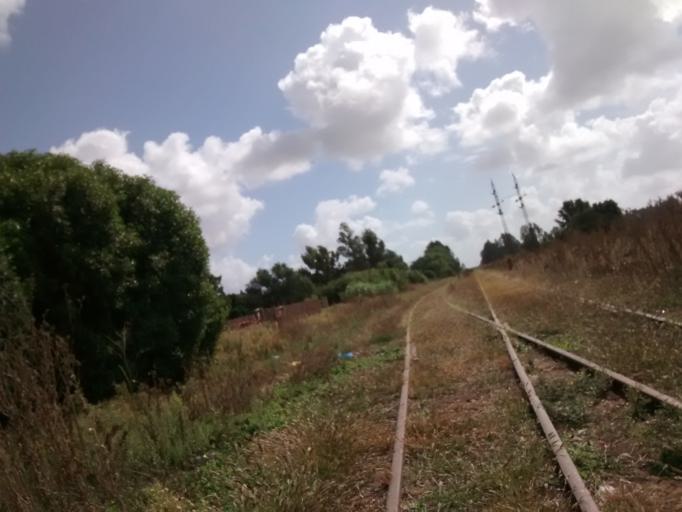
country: AR
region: Buenos Aires
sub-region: Partido de Loberia
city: Loberia
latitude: -38.1977
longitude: -58.7375
